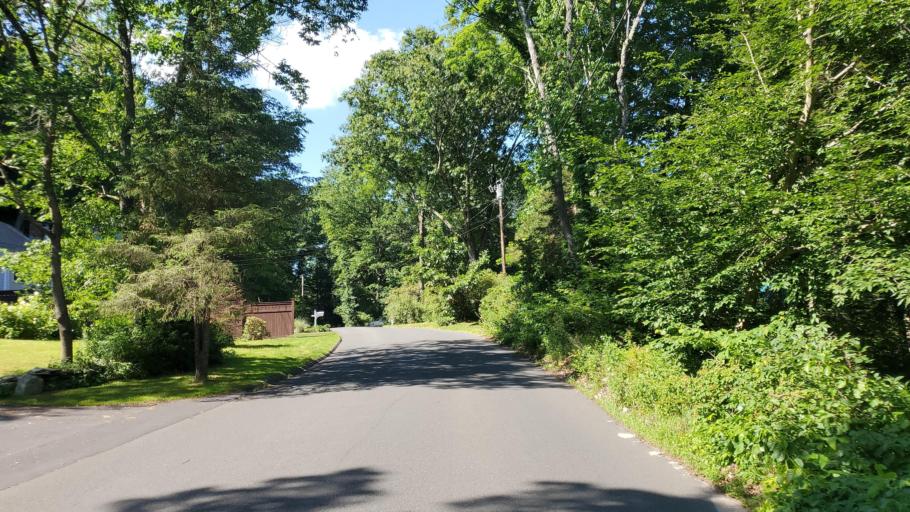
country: US
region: Connecticut
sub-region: Fairfield County
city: Newtown
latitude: 41.3368
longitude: -73.2918
